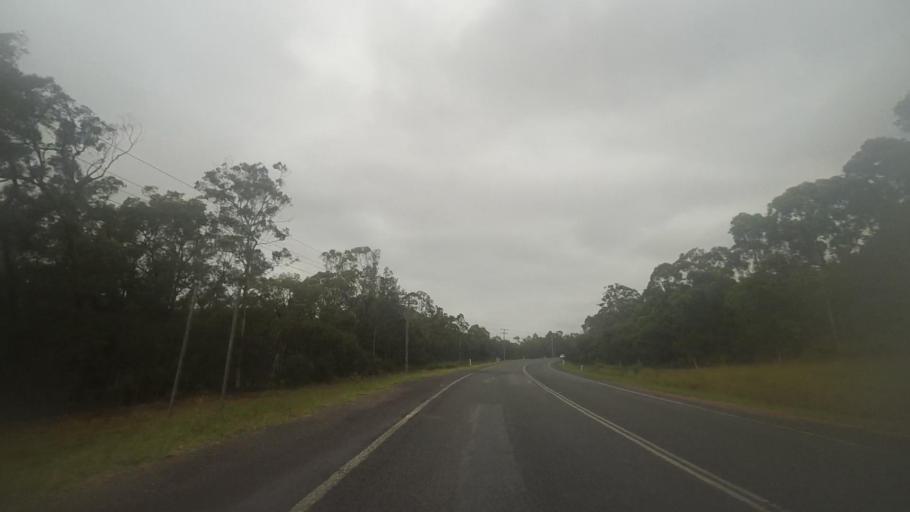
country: AU
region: New South Wales
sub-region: Port Stephens Shire
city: Port Stephens
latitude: -32.6370
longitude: 151.9947
